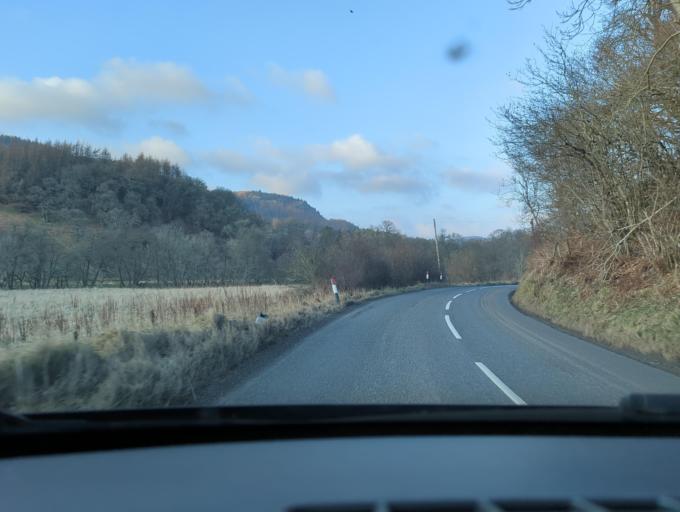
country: GB
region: Scotland
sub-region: Perth and Kinross
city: Methven
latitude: 56.5482
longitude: -3.6375
